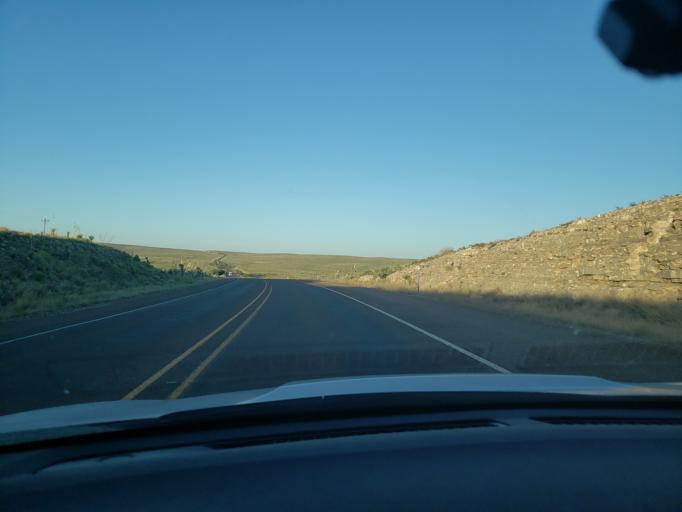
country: US
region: Texas
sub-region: El Paso County
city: Homestead Meadows South
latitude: 31.8269
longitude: -105.8791
